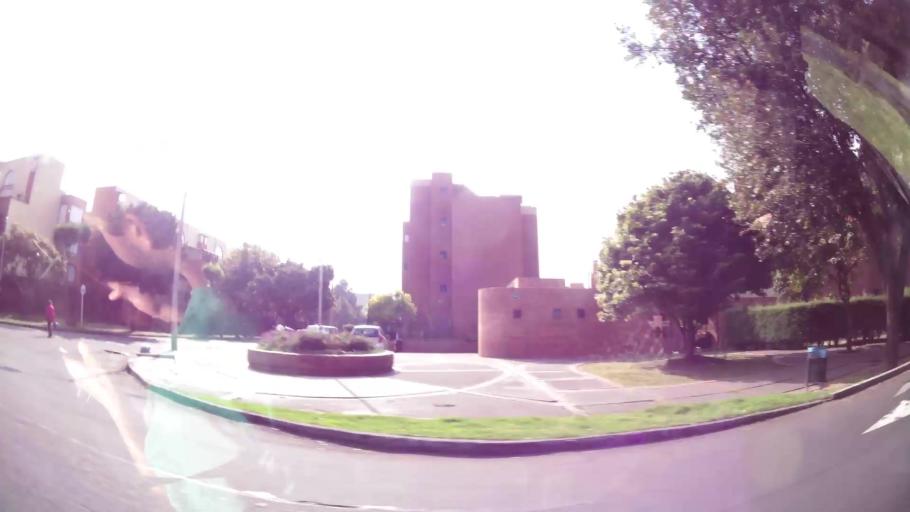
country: CO
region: Bogota D.C.
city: Barrio San Luis
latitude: 4.7316
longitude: -74.0633
